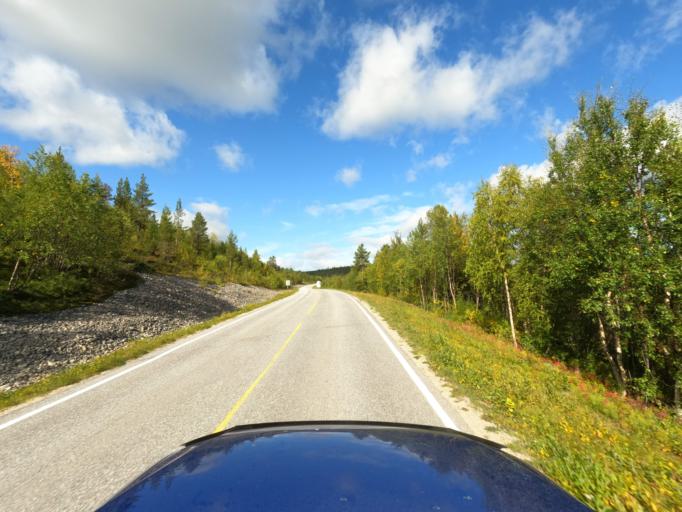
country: NO
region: Finnmark Fylke
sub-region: Karasjok
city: Karasjohka
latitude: 69.4840
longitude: 25.5102
